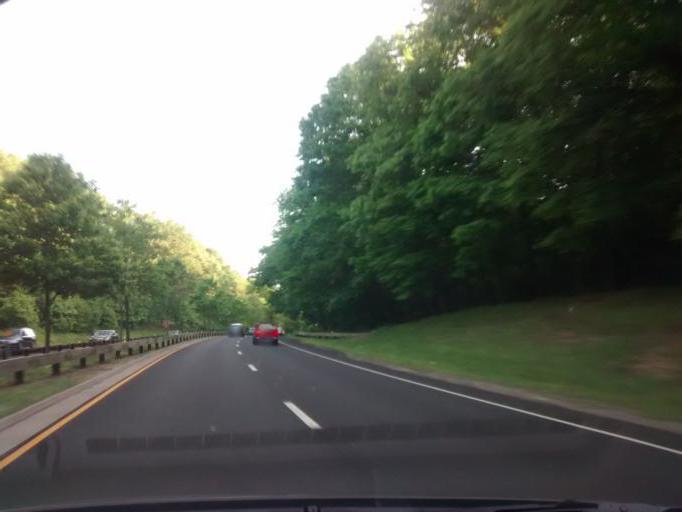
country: US
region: Connecticut
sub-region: Fairfield County
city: Glenville
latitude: 41.0822
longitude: -73.6658
